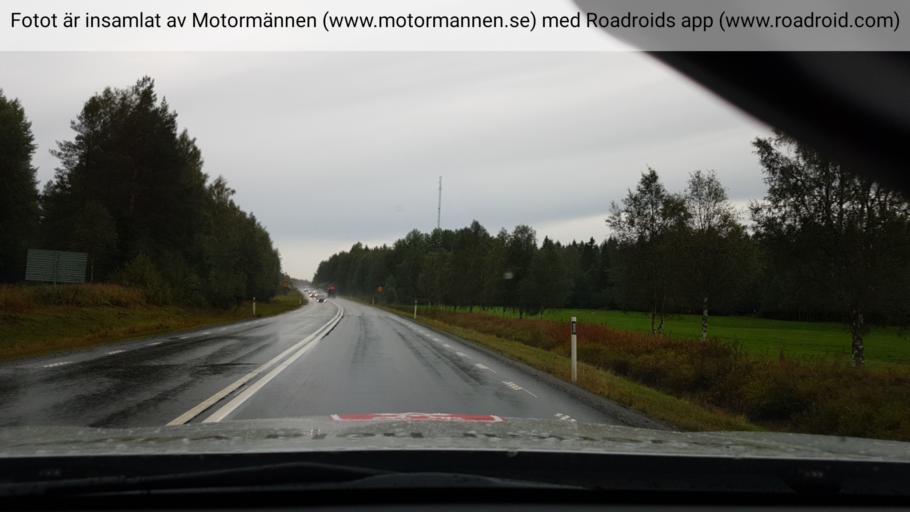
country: SE
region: Vaesterbotten
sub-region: Robertsfors Kommun
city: Robertsfors
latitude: 64.2690
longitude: 21.0466
